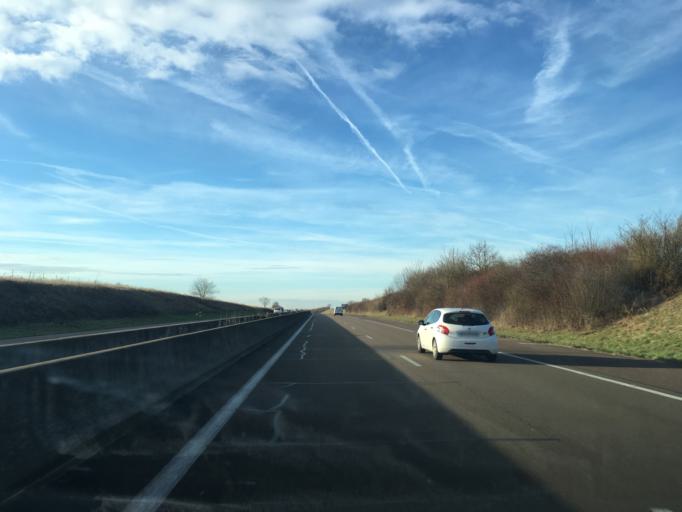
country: FR
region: Bourgogne
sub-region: Departement de l'Yonne
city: Avallon
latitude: 47.5003
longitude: 4.1084
